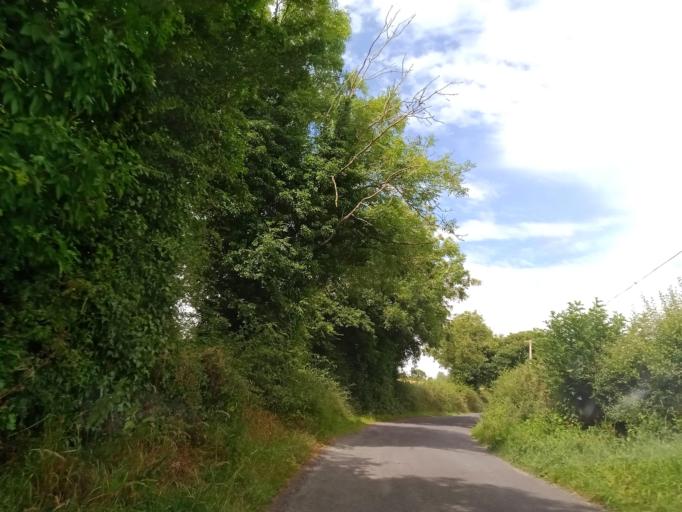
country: IE
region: Leinster
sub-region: Kilkenny
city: Thomastown
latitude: 52.5618
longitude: -7.1223
